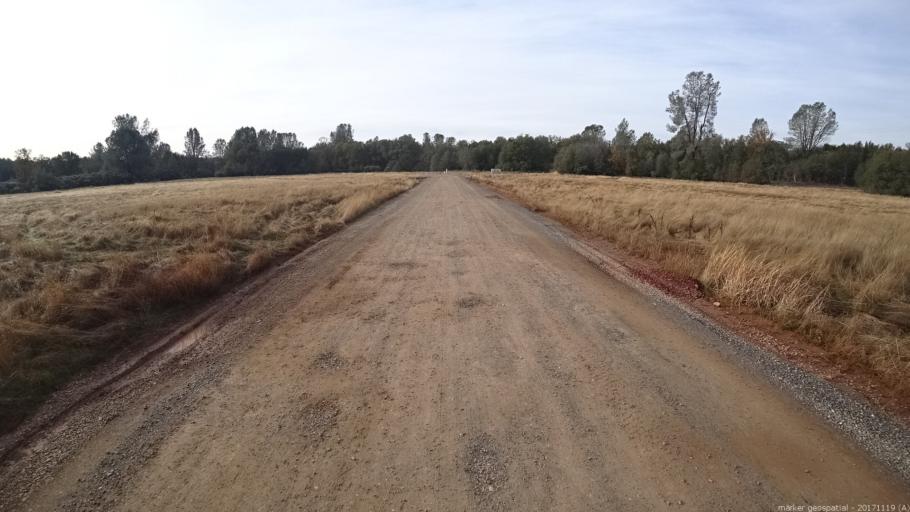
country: US
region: California
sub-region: Shasta County
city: Anderson
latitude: 40.5191
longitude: -122.3044
